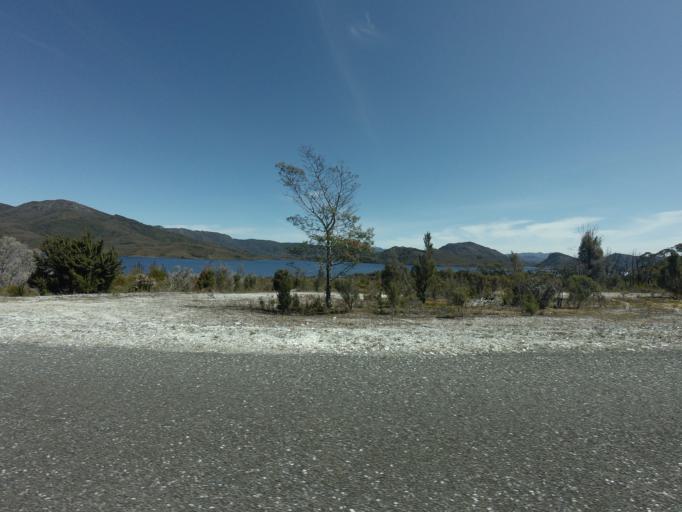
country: AU
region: Tasmania
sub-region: Huon Valley
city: Geeveston
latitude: -42.8436
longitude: 146.1648
